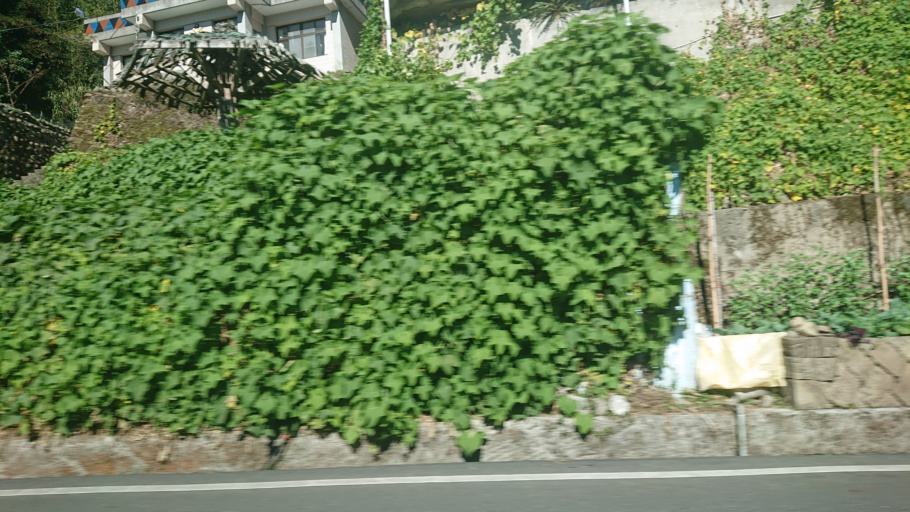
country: TW
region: Taiwan
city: Lugu
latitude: 23.4913
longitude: 120.7540
